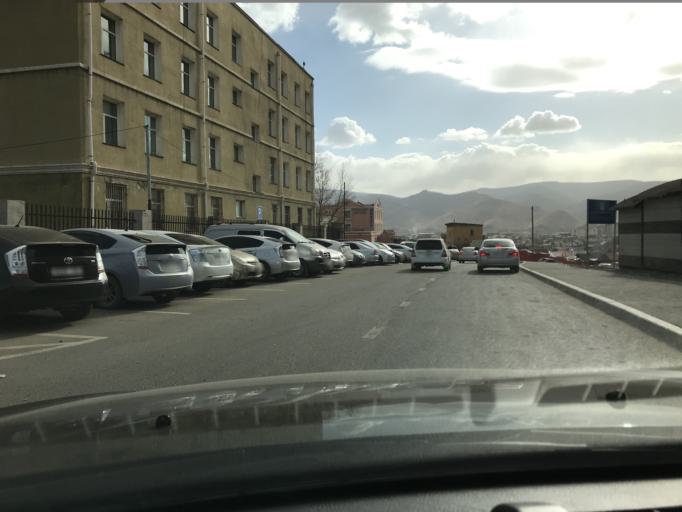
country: MN
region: Ulaanbaatar
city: Ulaanbaatar
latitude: 47.9163
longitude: 106.9642
